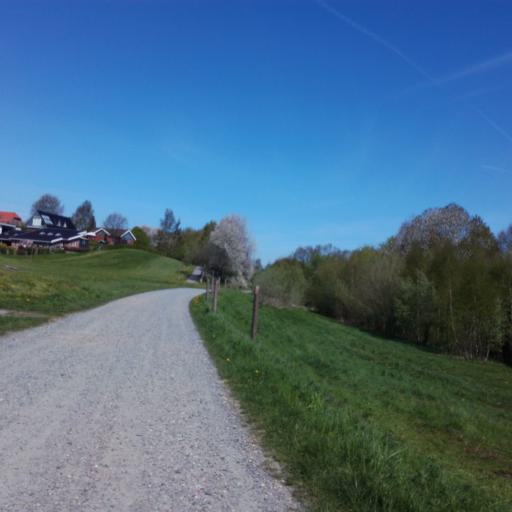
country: DK
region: South Denmark
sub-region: Vejle Kommune
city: Borkop
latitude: 55.6347
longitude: 9.6616
